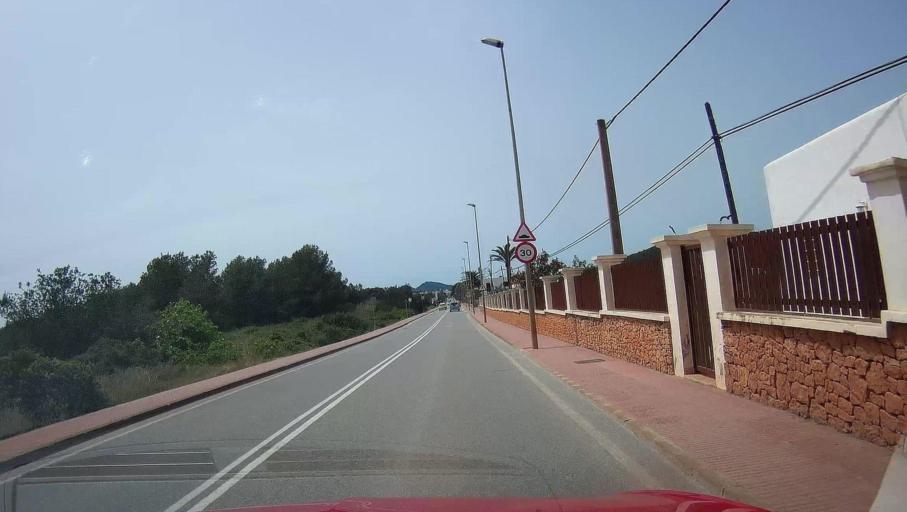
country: ES
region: Balearic Islands
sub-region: Illes Balears
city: Santa Eularia des Riu
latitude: 38.9950
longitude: 1.5529
